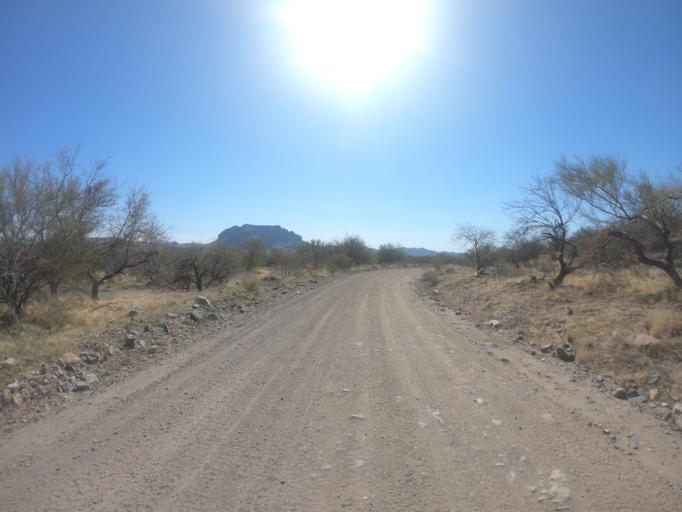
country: US
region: Arizona
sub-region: Pinal County
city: Superior
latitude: 33.2979
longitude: -111.1285
